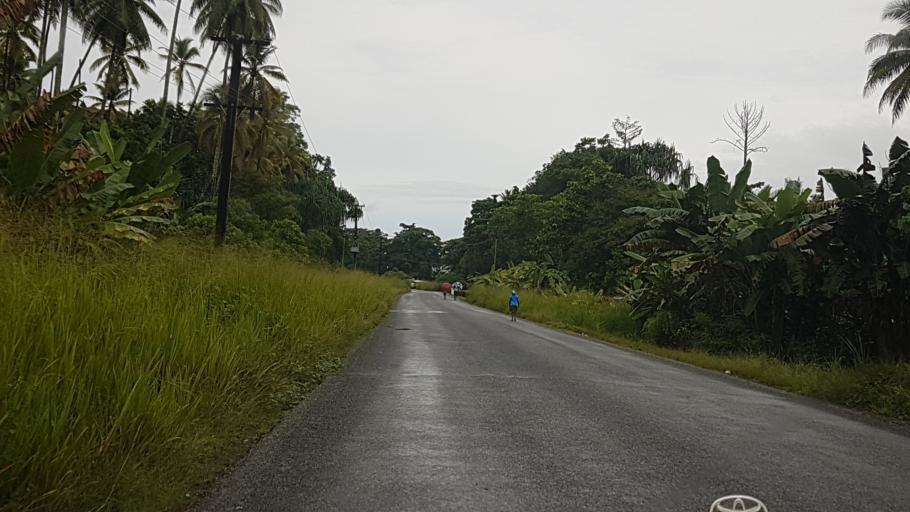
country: PG
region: Milne Bay
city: Alotau
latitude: -10.3085
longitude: 150.4218
